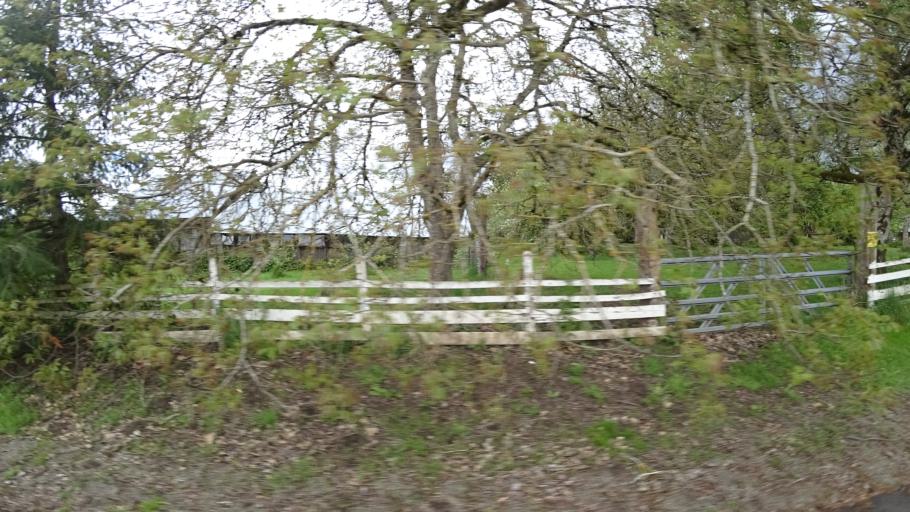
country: US
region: Oregon
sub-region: Washington County
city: Rockcreek
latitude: 45.5593
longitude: -122.9056
